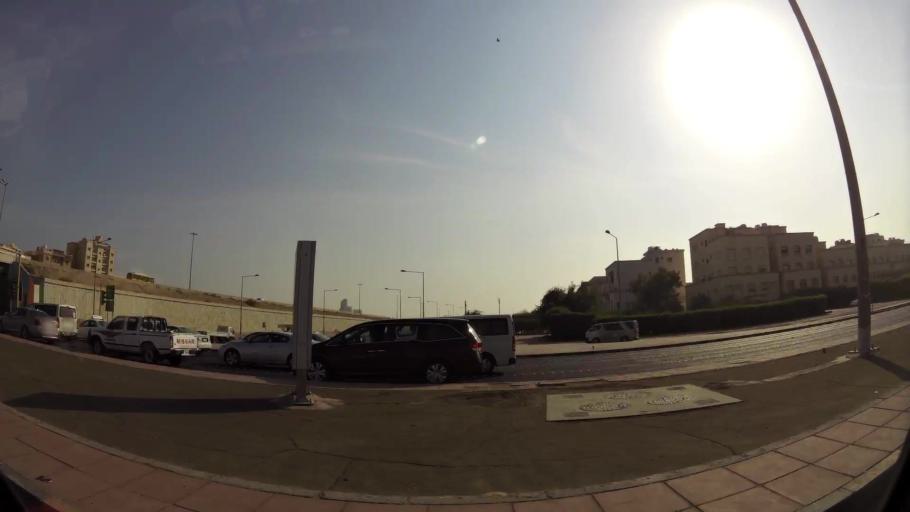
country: KW
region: Al Ahmadi
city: Al Fintas
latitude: 29.1719
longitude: 48.1117
